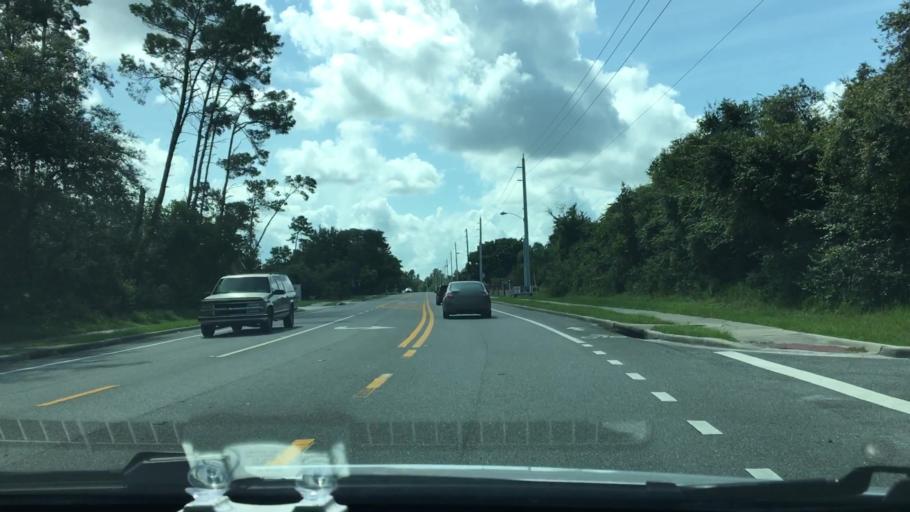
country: US
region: Florida
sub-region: Volusia County
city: Deltona
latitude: 28.8816
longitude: -81.2080
